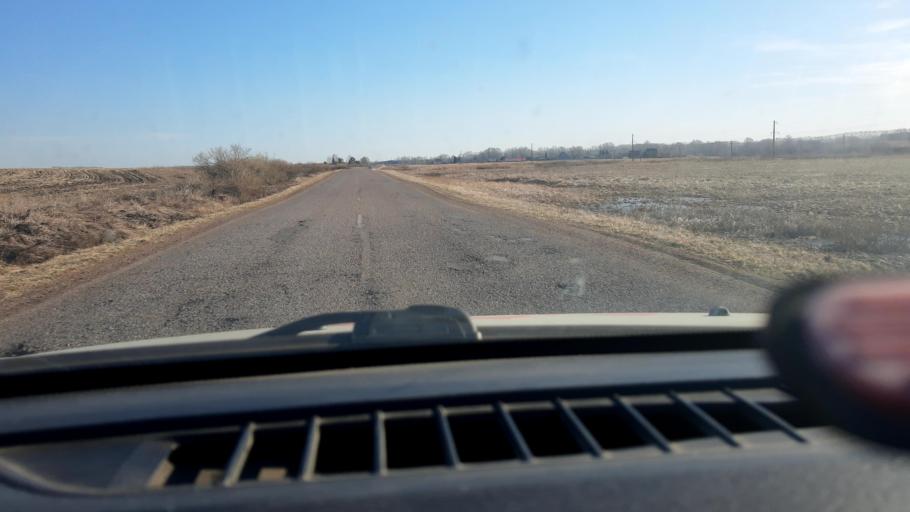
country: RU
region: Bashkortostan
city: Asanovo
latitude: 54.9165
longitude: 55.5059
